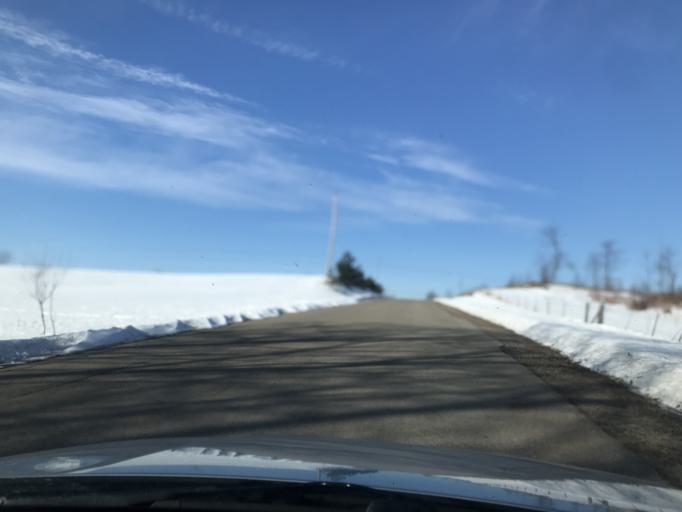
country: US
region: Wisconsin
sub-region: Oconto County
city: Gillett
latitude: 44.9394
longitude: -88.2380
